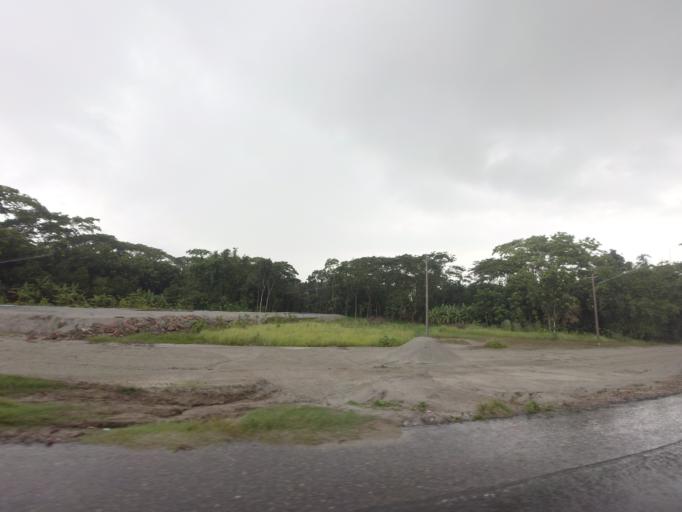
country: BD
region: Dhaka
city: Char Bhadrasan
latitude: 23.3756
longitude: 90.1029
